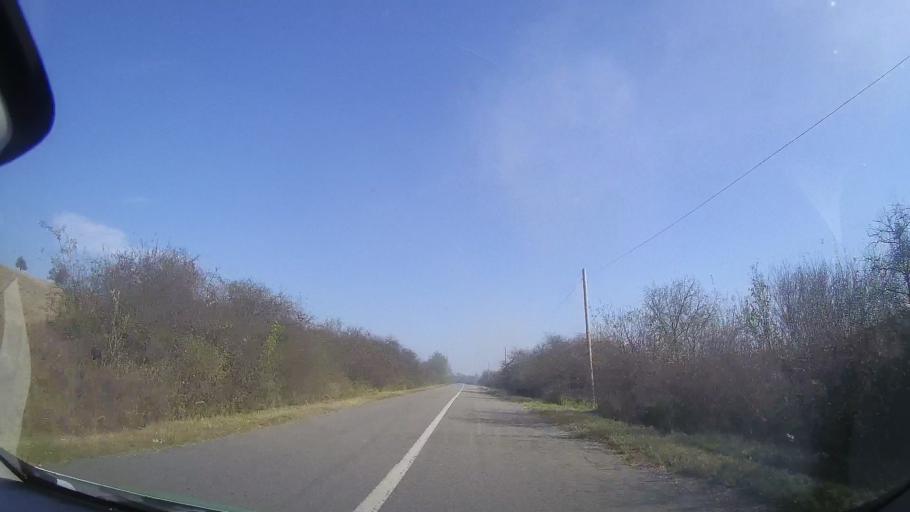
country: RO
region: Timis
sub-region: Comuna Secas
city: Secas
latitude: 45.8750
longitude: 21.8168
